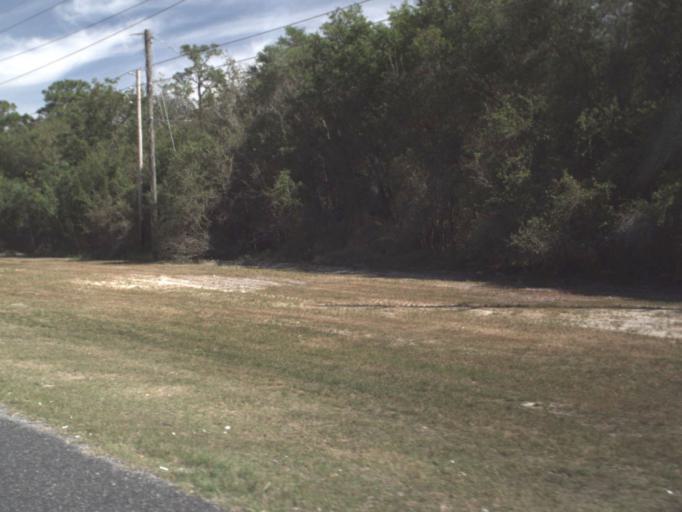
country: US
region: Florida
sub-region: Lake County
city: Lady Lake
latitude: 28.9097
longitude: -81.9180
